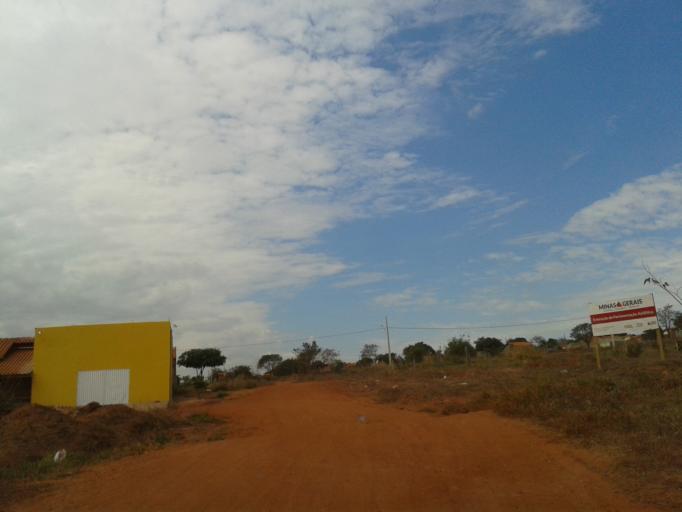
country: BR
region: Minas Gerais
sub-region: Santa Vitoria
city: Santa Vitoria
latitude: -18.8496
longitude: -50.1368
